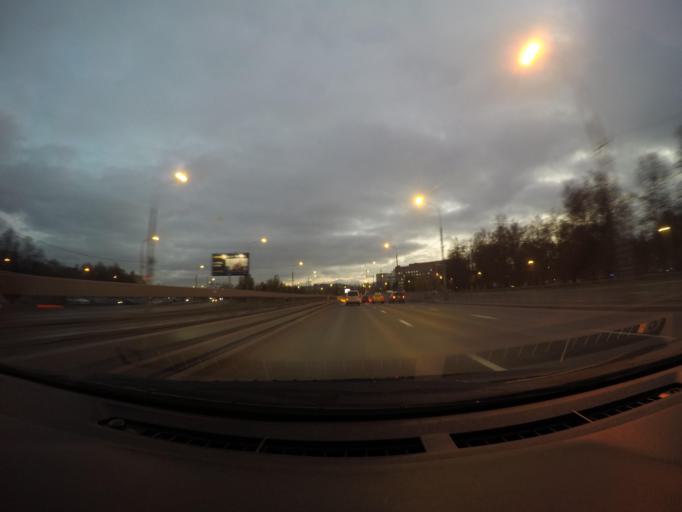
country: RU
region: Moscow
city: Tsaritsyno
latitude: 55.6554
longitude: 37.6532
